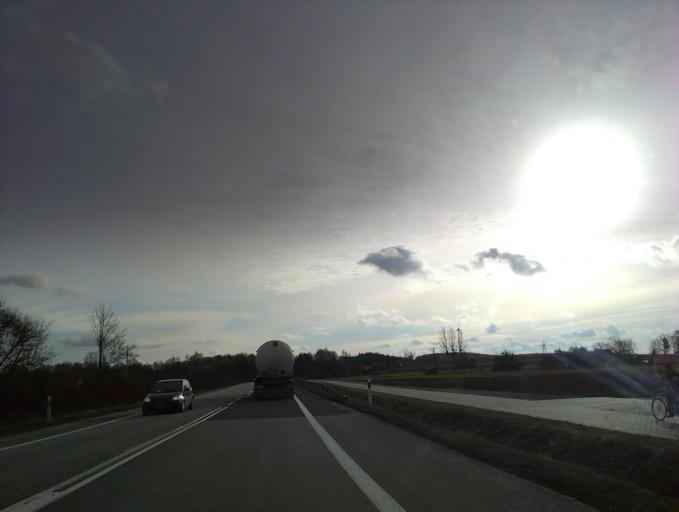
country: PL
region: Kujawsko-Pomorskie
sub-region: Powiat lipnowski
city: Kikol
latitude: 52.9016
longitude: 19.1212
